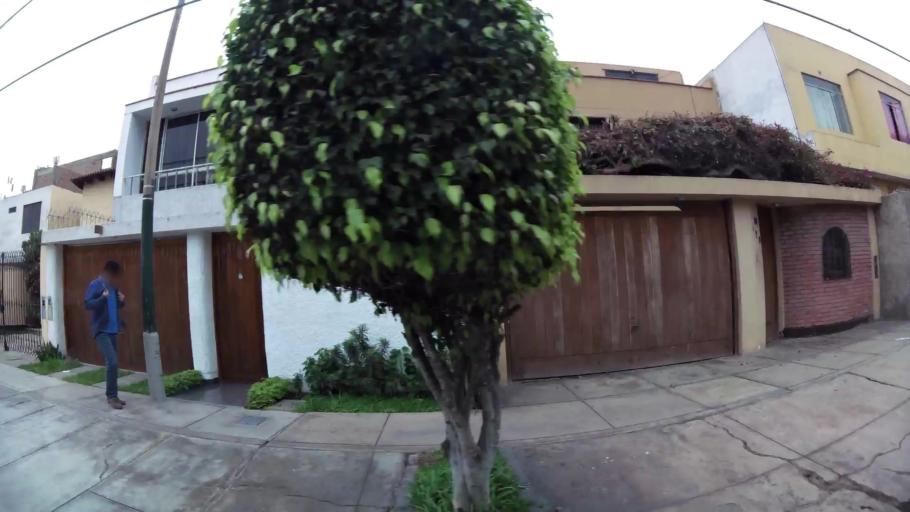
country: PE
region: Lima
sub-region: Lima
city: Surco
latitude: -12.1362
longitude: -77.0066
